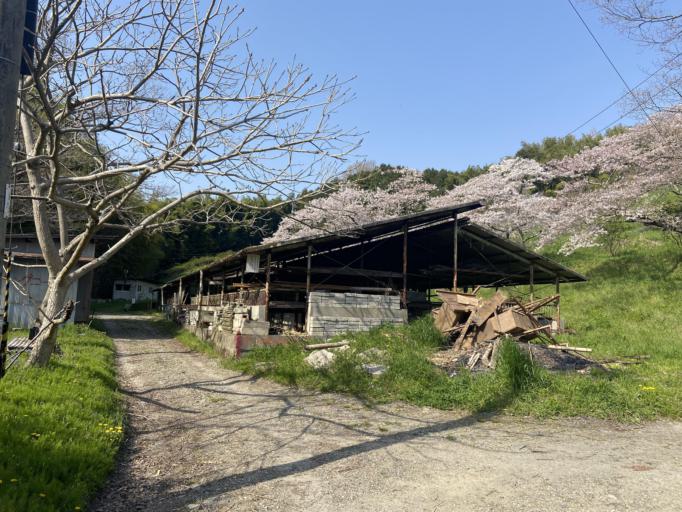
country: JP
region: Nara
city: Tenri
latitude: 34.6123
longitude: 135.8478
